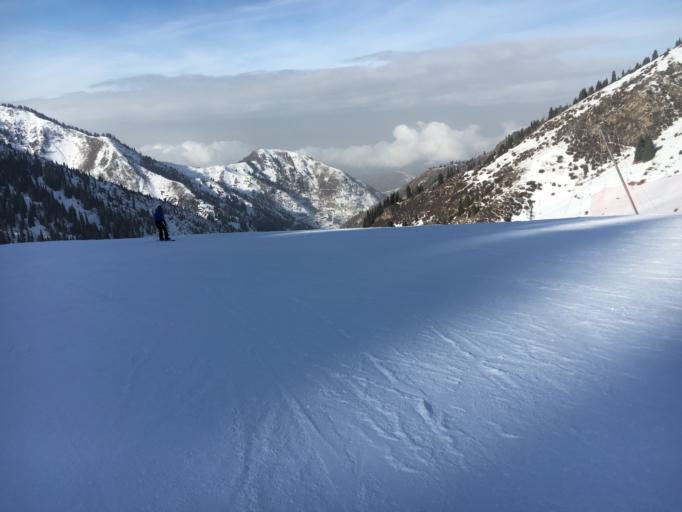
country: KZ
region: Almaty Qalasy
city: Almaty
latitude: 43.1255
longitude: 77.0888
